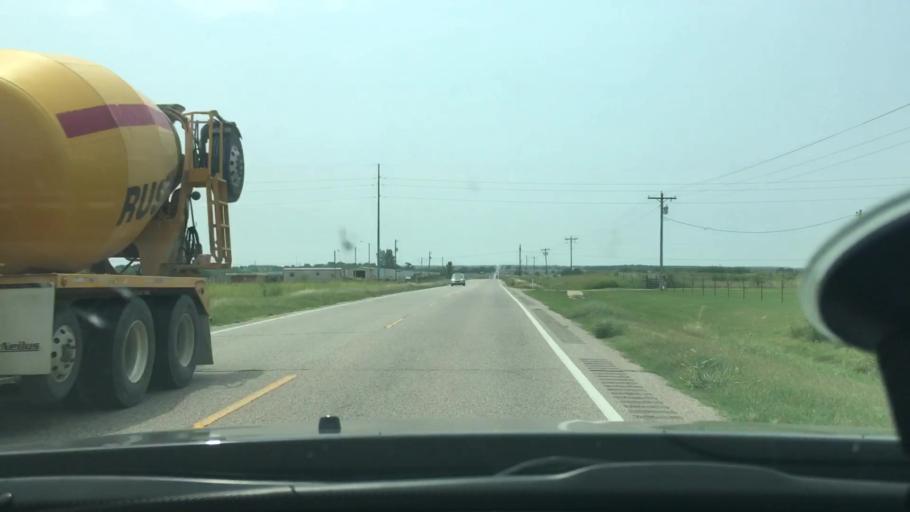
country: US
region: Oklahoma
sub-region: Marshall County
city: Kingston
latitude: 34.0144
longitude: -96.7611
